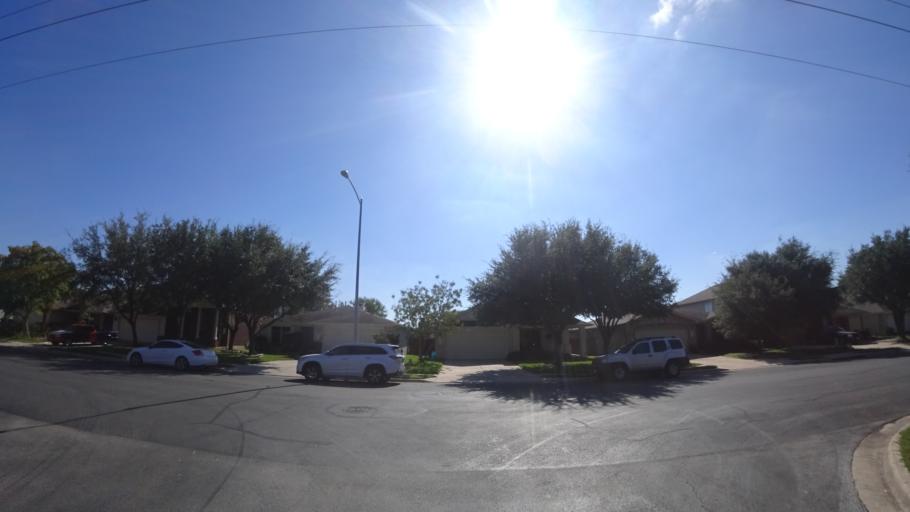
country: US
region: Texas
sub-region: Travis County
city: Manor
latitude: 30.3641
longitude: -97.6112
